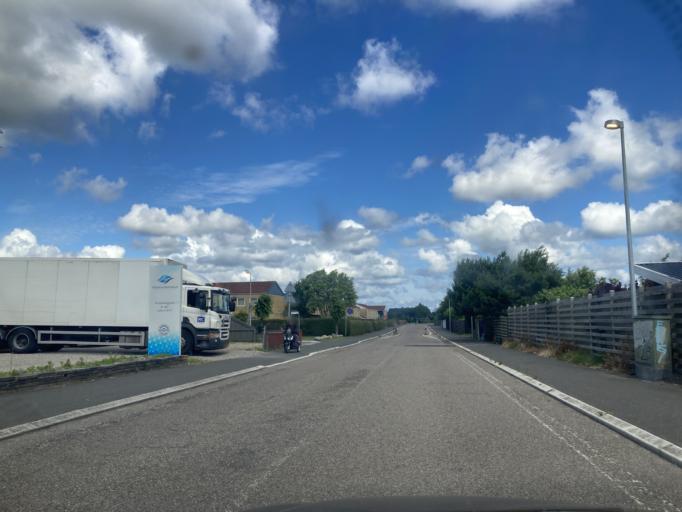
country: DK
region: Capital Region
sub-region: Halsnaes Kommune
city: Frederiksvaerk
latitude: 55.9813
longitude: 12.0149
